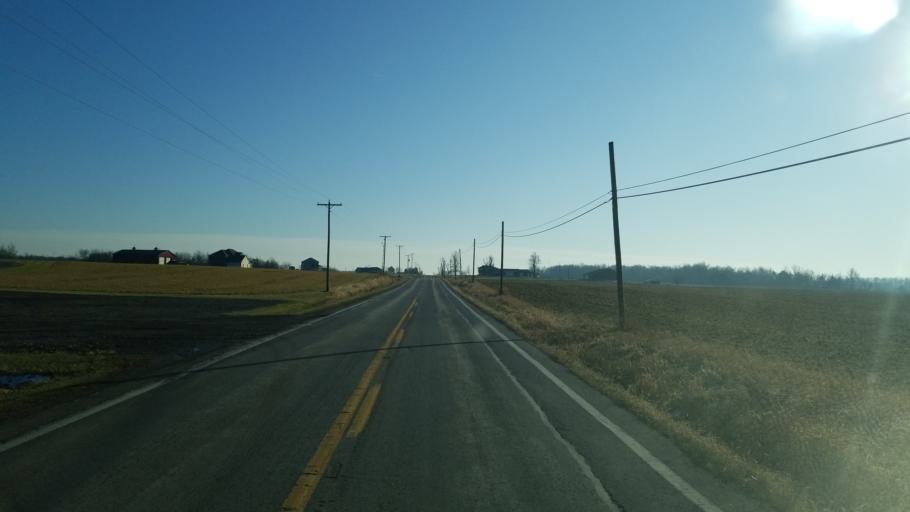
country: US
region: Ohio
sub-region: Sandusky County
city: Green Springs
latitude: 41.1164
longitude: -83.0156
